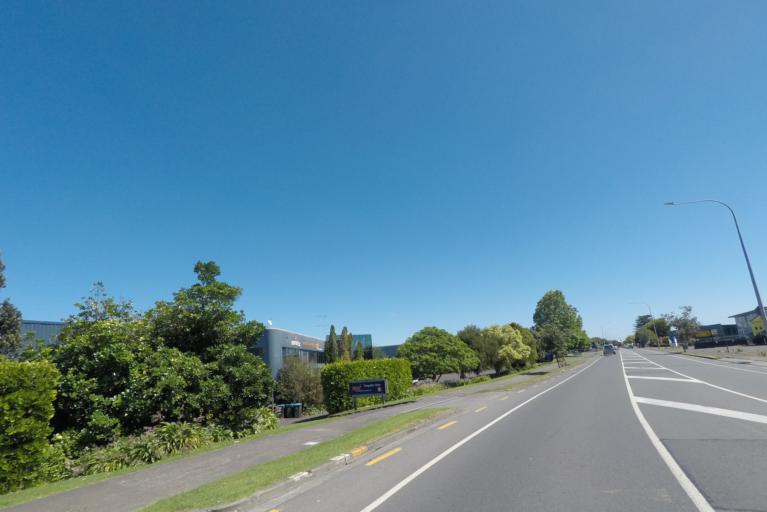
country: NZ
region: Auckland
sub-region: Auckland
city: Rosebank
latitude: -36.8775
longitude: 174.6700
